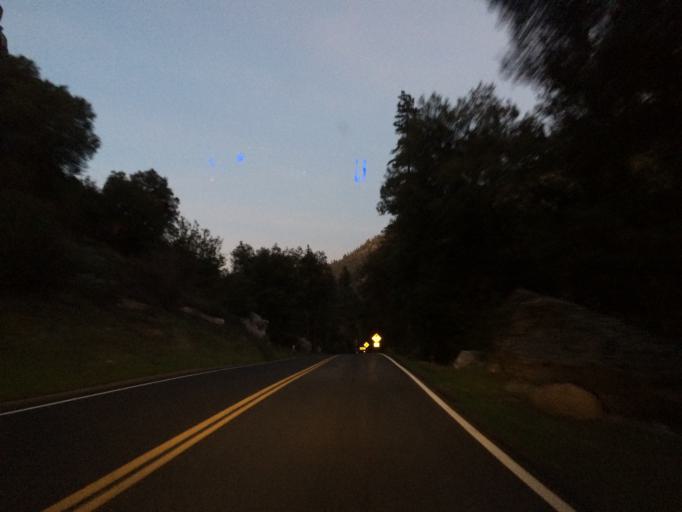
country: US
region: California
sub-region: Mariposa County
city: Yosemite Valley
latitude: 37.6845
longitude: -119.7325
